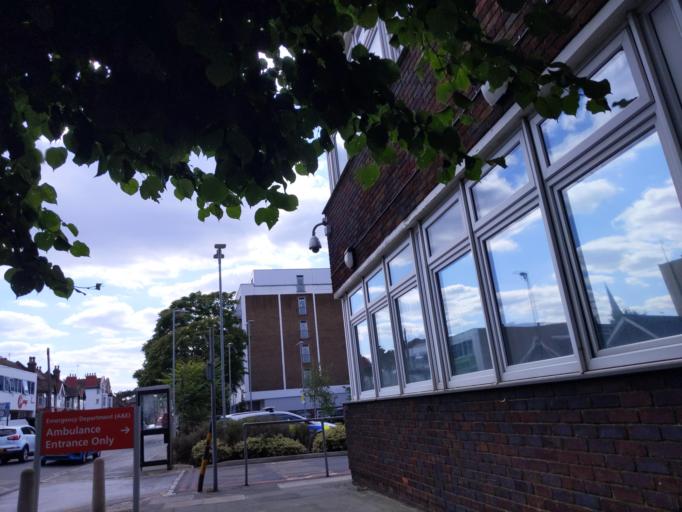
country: GB
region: England
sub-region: Greater London
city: Croydon
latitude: 51.3886
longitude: -0.1084
